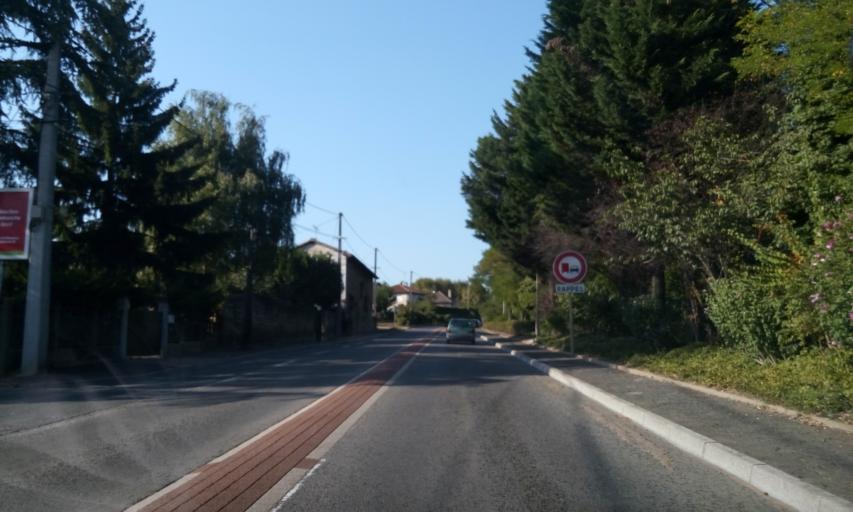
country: FR
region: Rhone-Alpes
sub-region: Departement du Rhone
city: Anse
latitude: 45.9446
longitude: 4.7147
